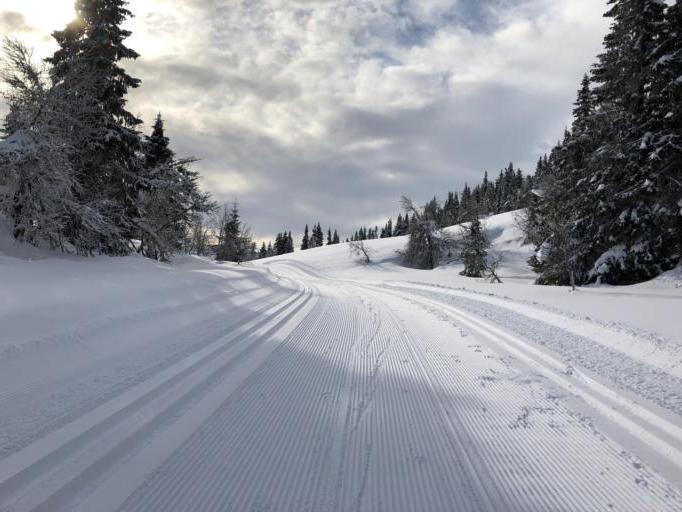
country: NO
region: Oppland
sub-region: Gausdal
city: Segalstad bru
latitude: 61.3194
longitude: 10.0578
